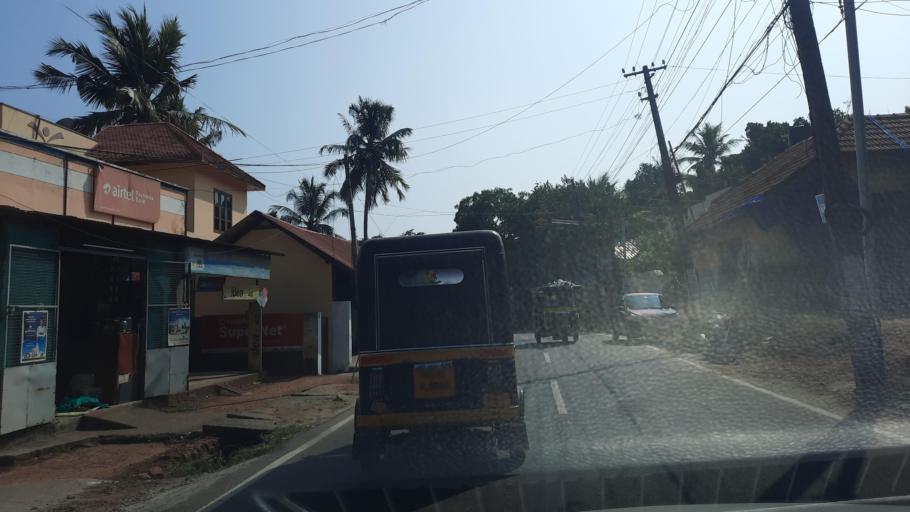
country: IN
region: Kerala
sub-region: Thiruvananthapuram
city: Thiruvananthapuram
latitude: 8.5658
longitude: 76.9218
